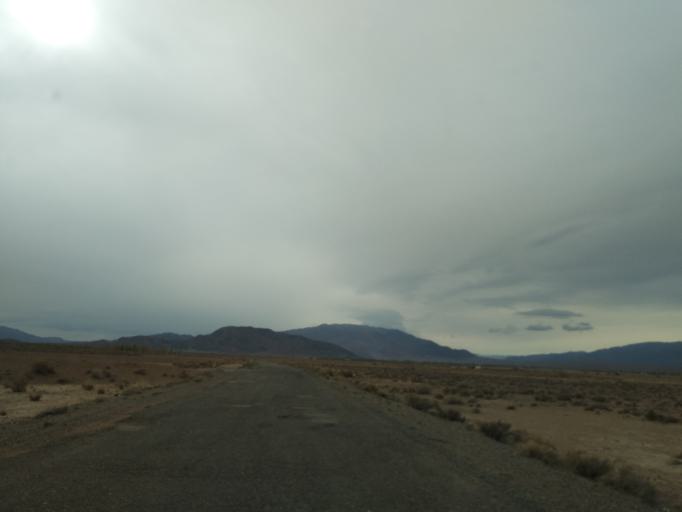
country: KG
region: Ysyk-Koel
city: Balykchy
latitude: 42.3202
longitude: 76.2242
